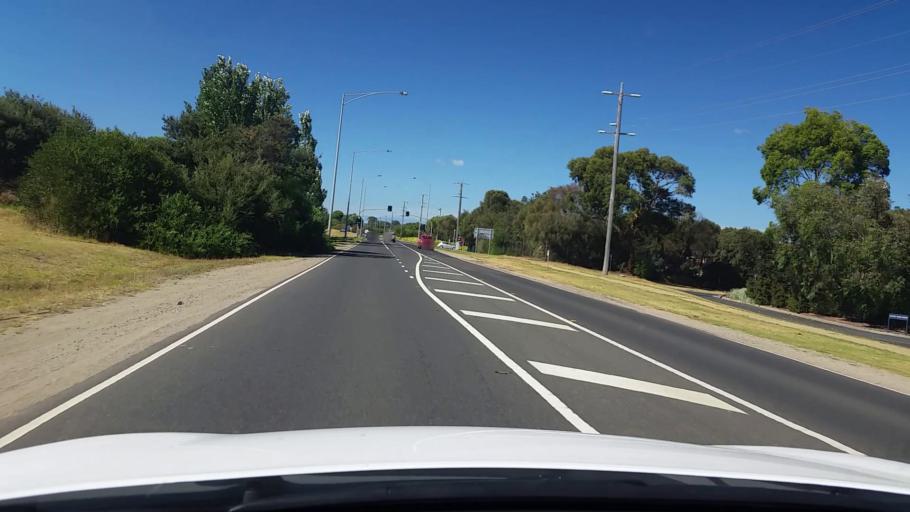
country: AU
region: Victoria
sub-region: Mornington Peninsula
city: Rosebud West
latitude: -38.3841
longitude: 144.8887
